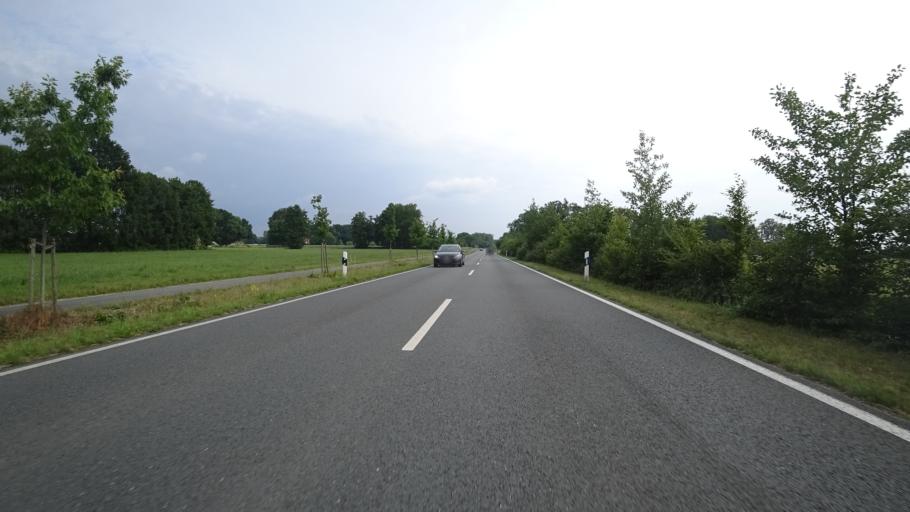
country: DE
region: North Rhine-Westphalia
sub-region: Regierungsbezirk Detmold
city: Guetersloh
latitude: 51.9544
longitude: 8.3802
